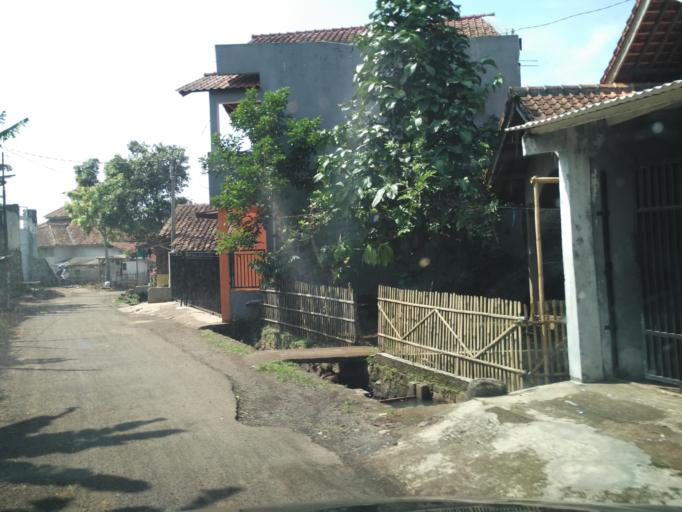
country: ID
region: West Java
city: Ciranjang-hilir
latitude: -6.8018
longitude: 107.1247
